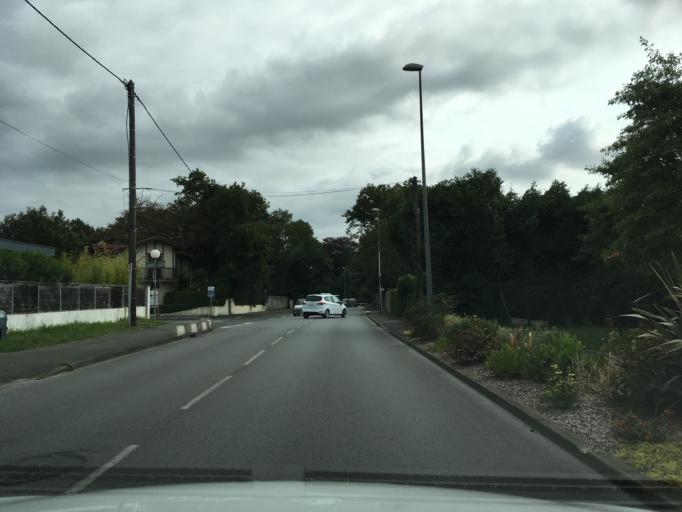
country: FR
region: Aquitaine
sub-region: Departement des Pyrenees-Atlantiques
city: Anglet
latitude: 43.4932
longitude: -1.5156
